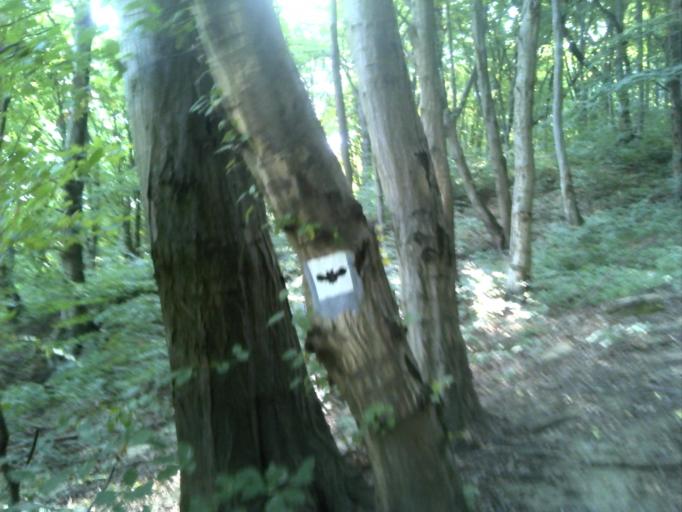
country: HU
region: Baranya
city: Pellerd
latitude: 46.1367
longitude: 18.1179
